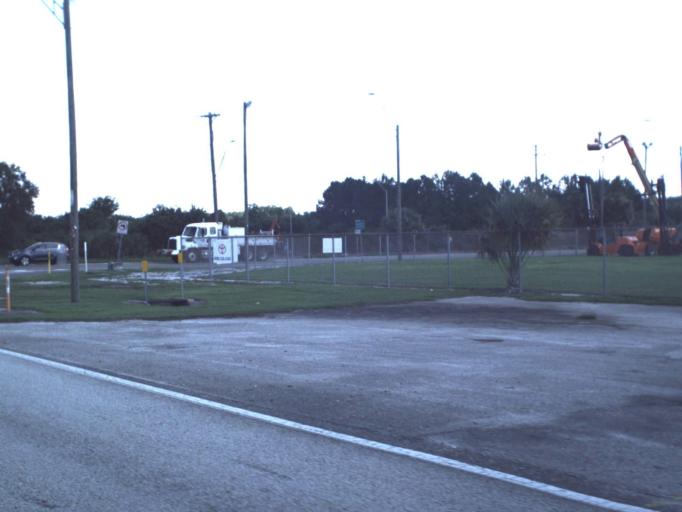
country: US
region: Florida
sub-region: Hillsborough County
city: Palm River-Clair Mel
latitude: 27.9522
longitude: -82.3697
